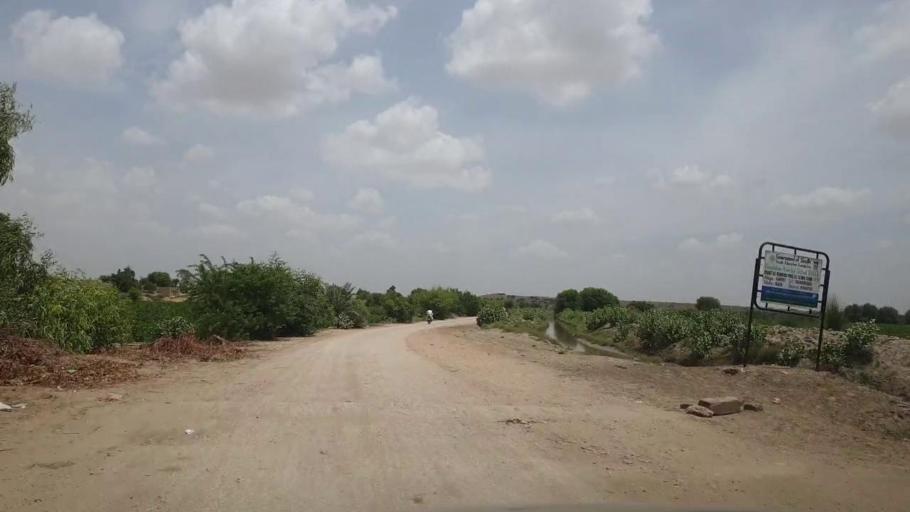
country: PK
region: Sindh
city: Kot Diji
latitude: 27.2009
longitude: 69.0598
